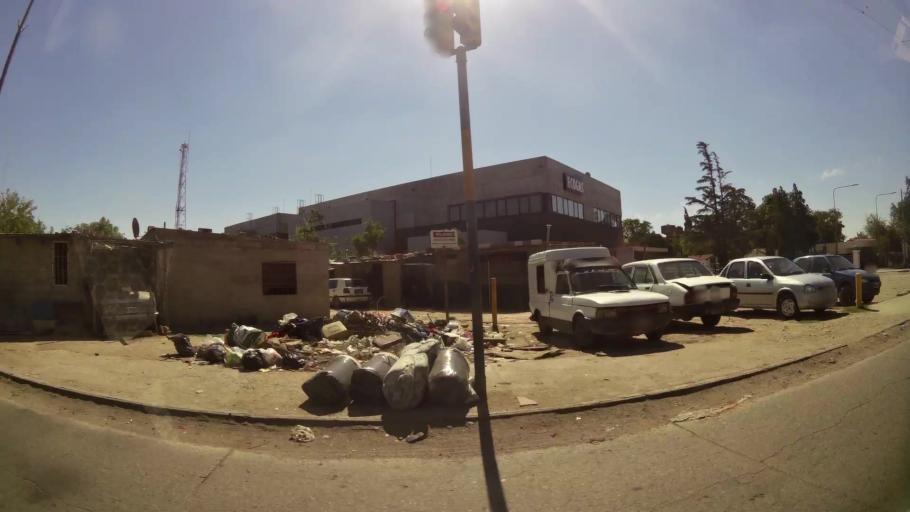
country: AR
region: Cordoba
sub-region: Departamento de Capital
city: Cordoba
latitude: -31.3740
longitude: -64.1761
